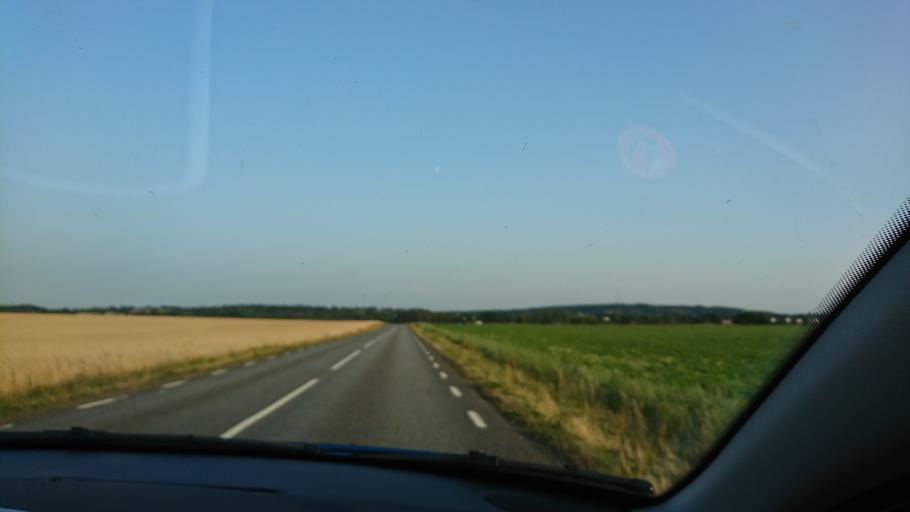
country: SE
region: Skane
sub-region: Simrishamns Kommun
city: Kivik
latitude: 55.6960
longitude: 14.1550
